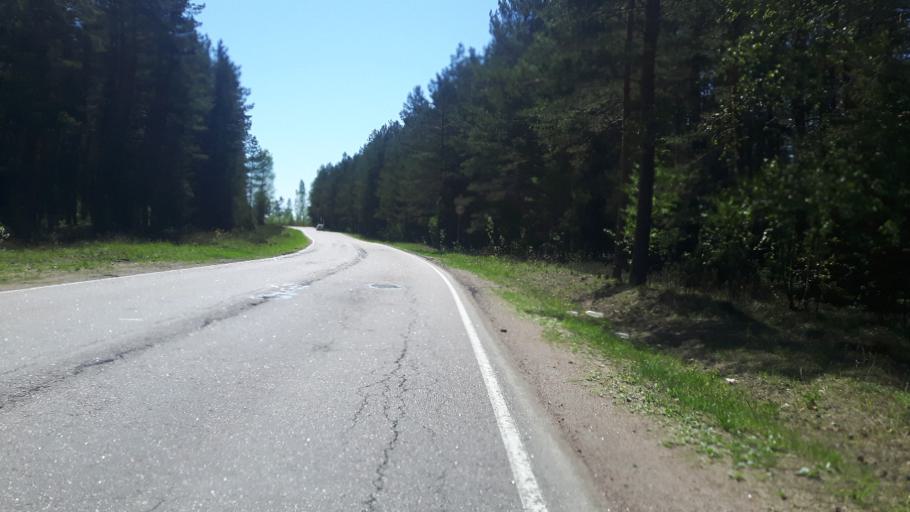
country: RU
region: Leningrad
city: Glebychevo
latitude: 60.3358
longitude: 28.8214
